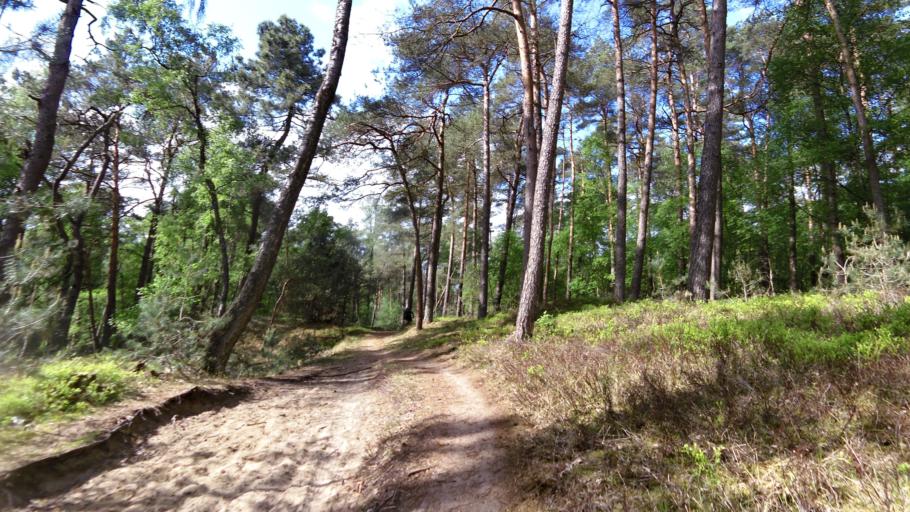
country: NL
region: Gelderland
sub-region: Gemeente Brummen
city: Eerbeek
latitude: 52.0790
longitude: 6.0456
